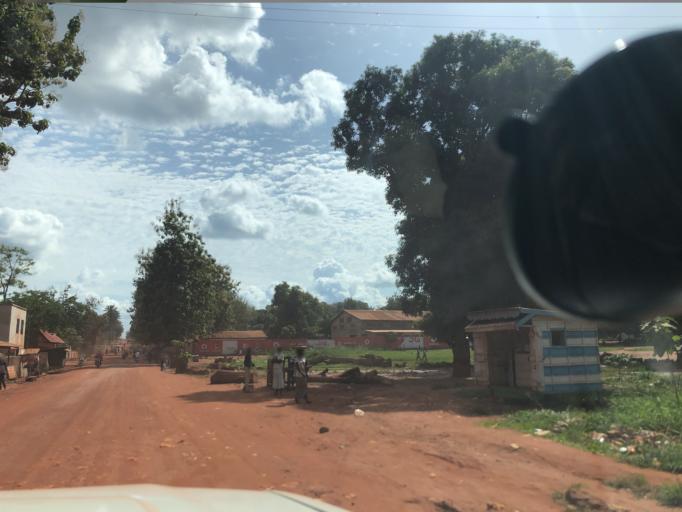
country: CD
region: Equateur
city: Gemena
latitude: 3.2454
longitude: 19.7827
